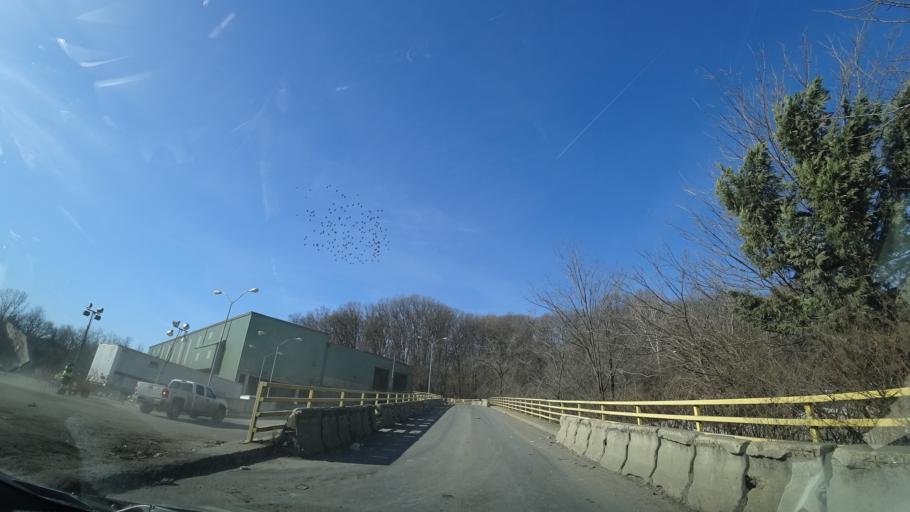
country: US
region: Maryland
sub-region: Prince George's County
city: Chillum
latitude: 38.9482
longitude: -77.0017
